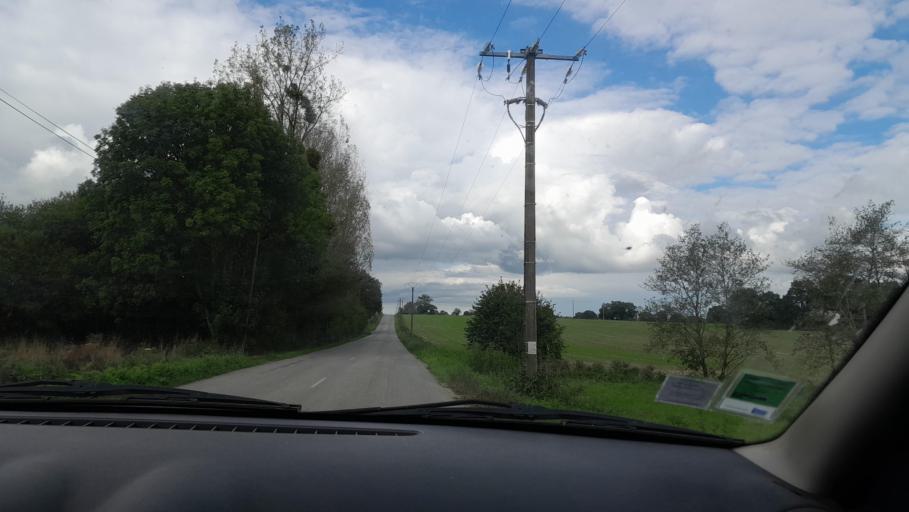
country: FR
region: Brittany
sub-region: Departement d'Ille-et-Vilaine
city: Le Pertre
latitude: 47.9958
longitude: -1.0399
